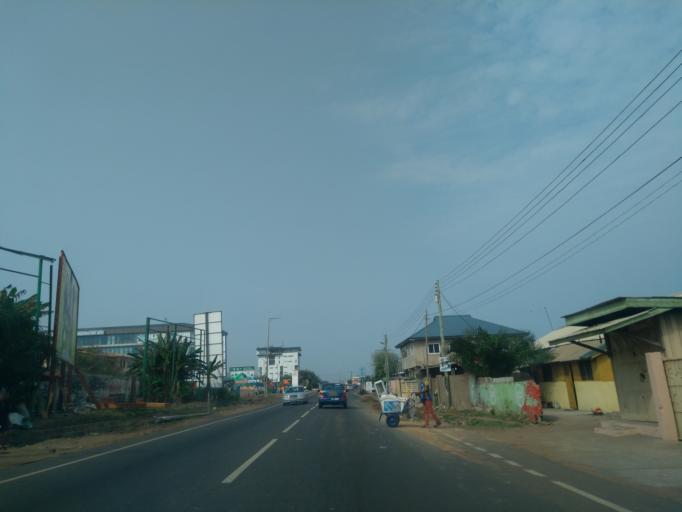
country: GH
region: Greater Accra
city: Accra
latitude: 5.5541
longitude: -0.1734
